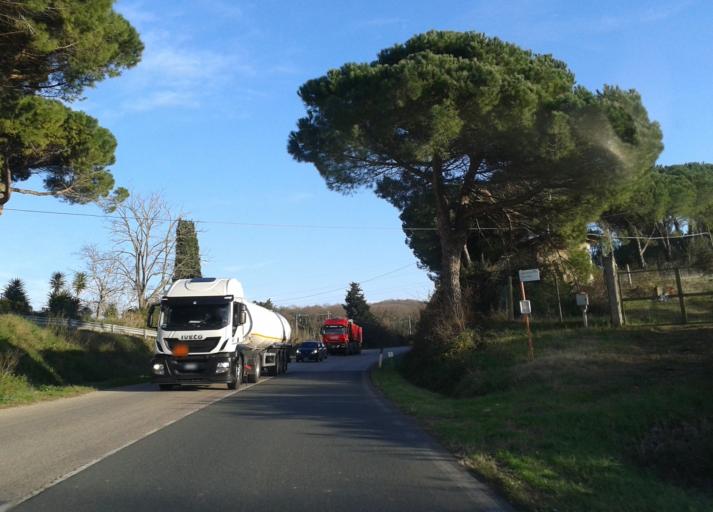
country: IT
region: Tuscany
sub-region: Provincia di Livorno
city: Guasticce
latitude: 43.5729
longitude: 10.3740
